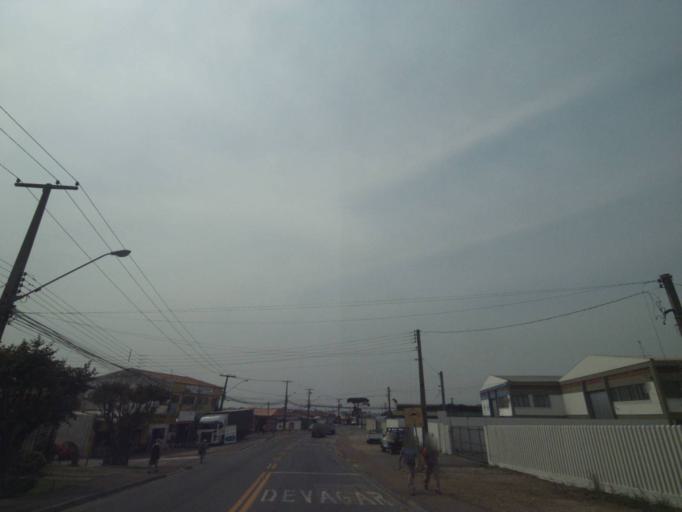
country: BR
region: Parana
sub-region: Sao Jose Dos Pinhais
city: Sao Jose dos Pinhais
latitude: -25.5216
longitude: -49.2886
